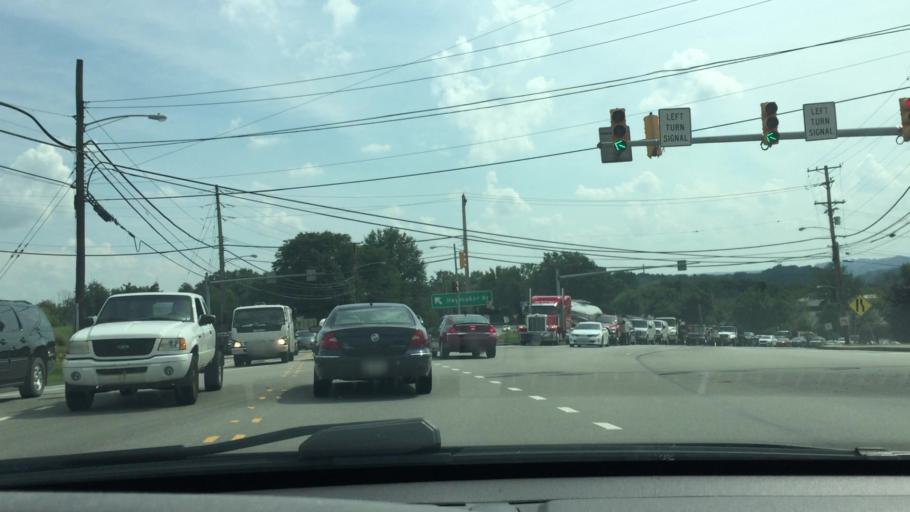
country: US
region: Pennsylvania
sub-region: Allegheny County
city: Monroeville
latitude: 40.4298
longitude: -79.7512
